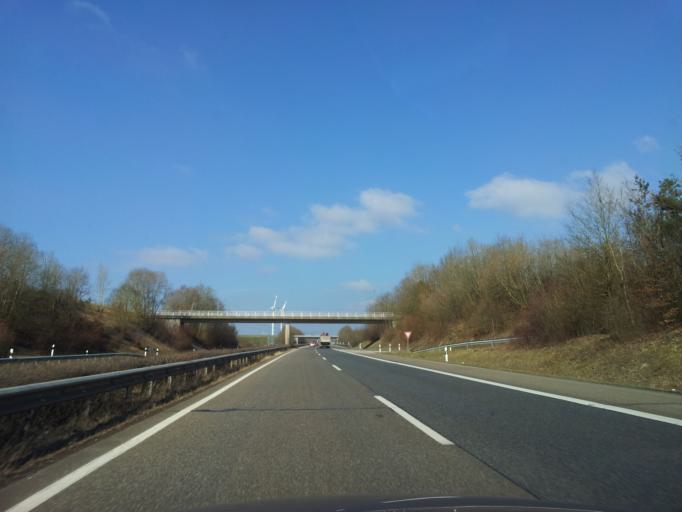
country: DE
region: Rheinland-Pfalz
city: Schleid
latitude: 50.0509
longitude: 6.4903
